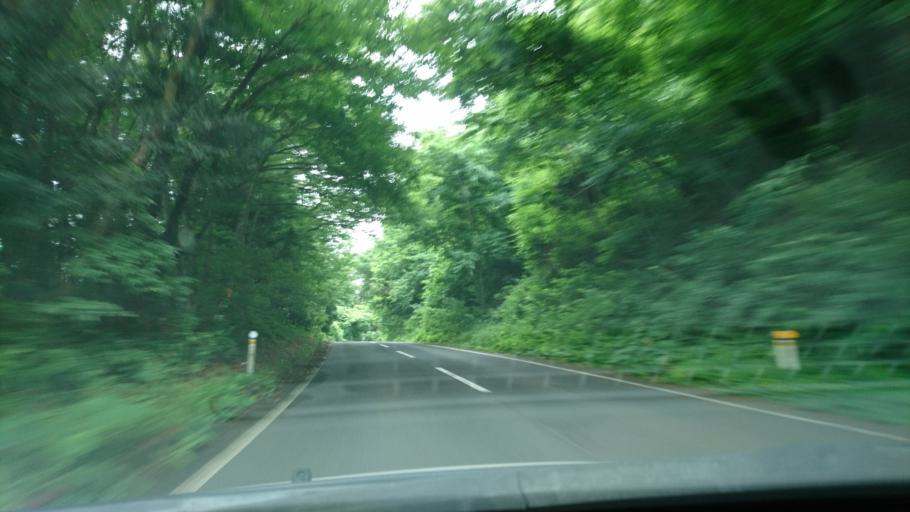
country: JP
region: Iwate
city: Ichinoseki
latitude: 38.9455
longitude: 141.2804
